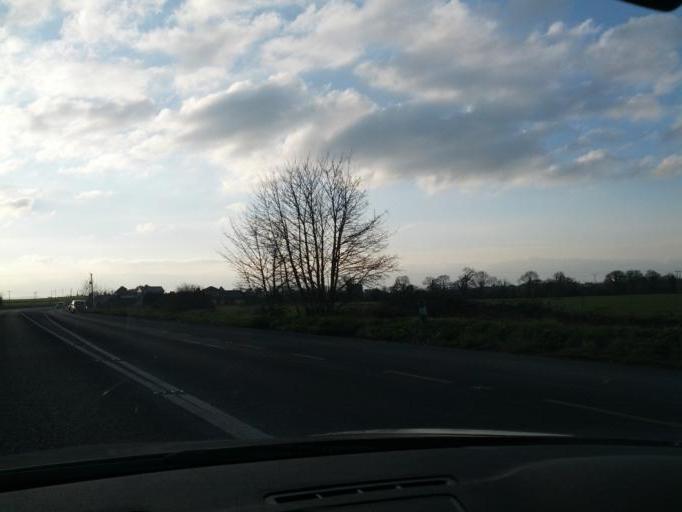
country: IE
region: Munster
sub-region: North Tipperary
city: Nenagh
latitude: 52.8625
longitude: -8.1547
